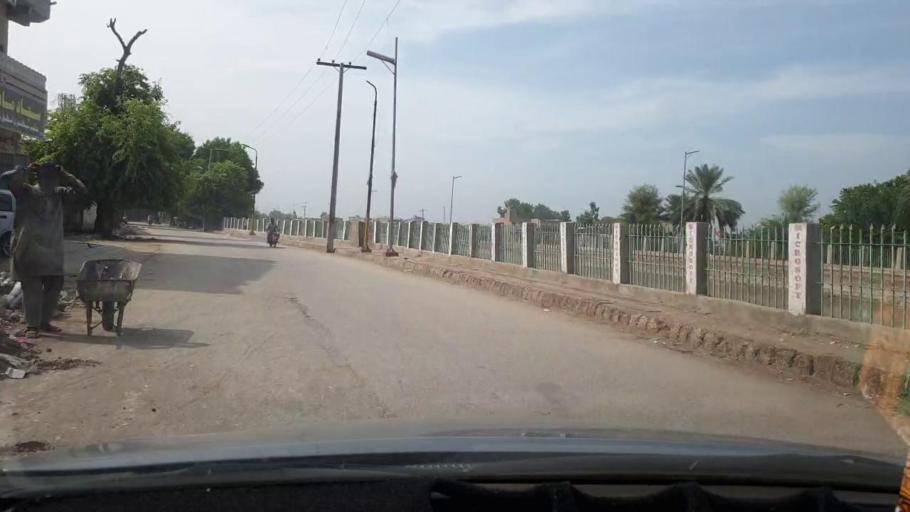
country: PK
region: Sindh
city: Khairpur
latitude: 27.5310
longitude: 68.7530
